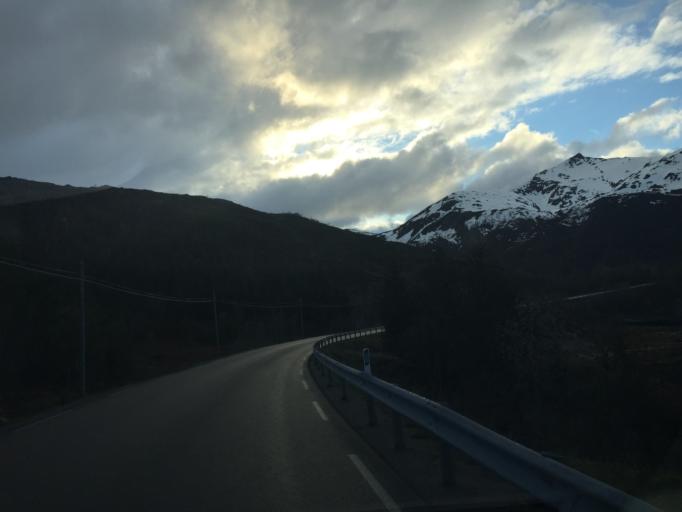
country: NO
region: Nordland
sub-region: Vagan
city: Svolvaer
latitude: 68.3191
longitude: 14.7021
